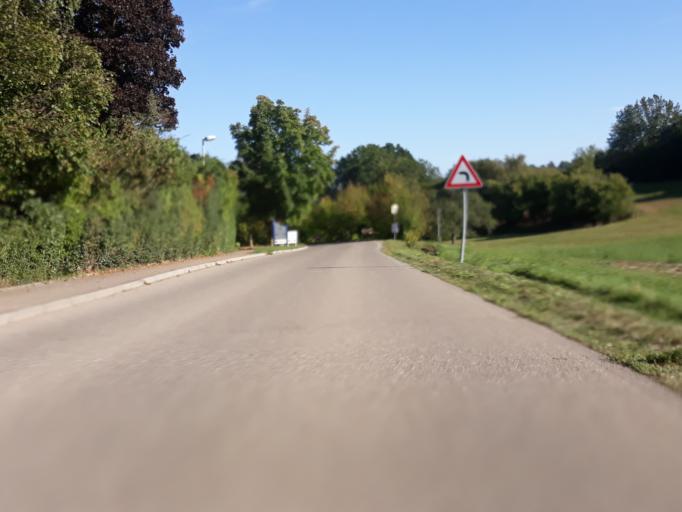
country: DE
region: Baden-Wuerttemberg
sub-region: Karlsruhe Region
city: Gechingen
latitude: 48.6836
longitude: 8.8472
